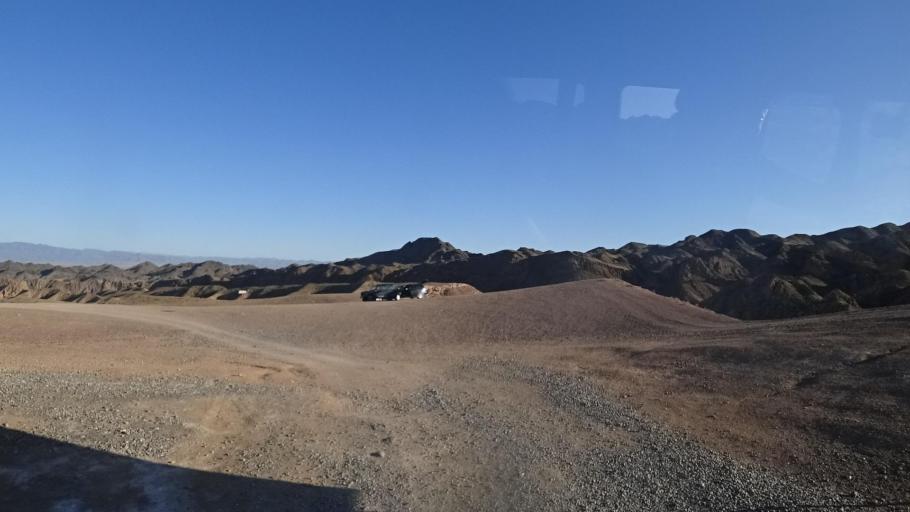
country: KZ
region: Almaty Oblysy
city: Kegen
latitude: 43.3561
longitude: 79.0539
